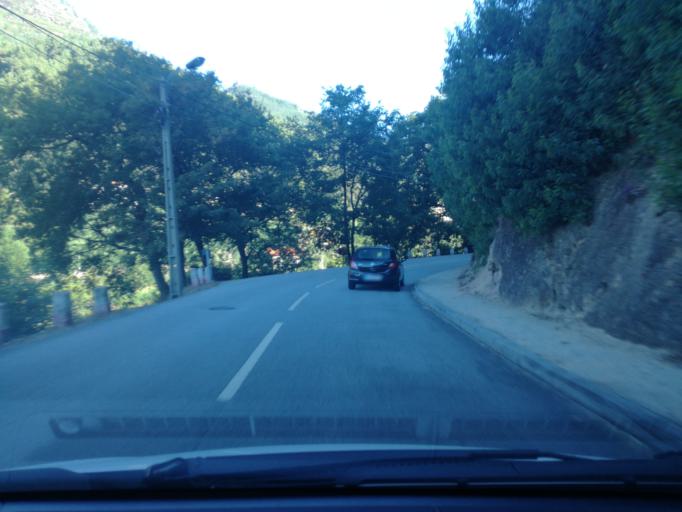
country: PT
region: Braga
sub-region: Vieira do Minho
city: Real
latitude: 41.7216
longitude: -8.1639
